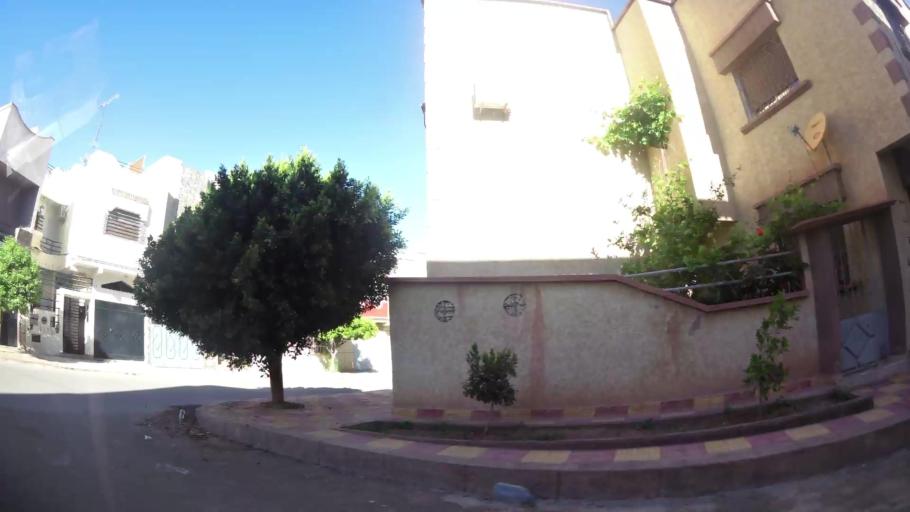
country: MA
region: Oriental
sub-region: Oujda-Angad
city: Oujda
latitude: 34.6611
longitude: -1.9026
